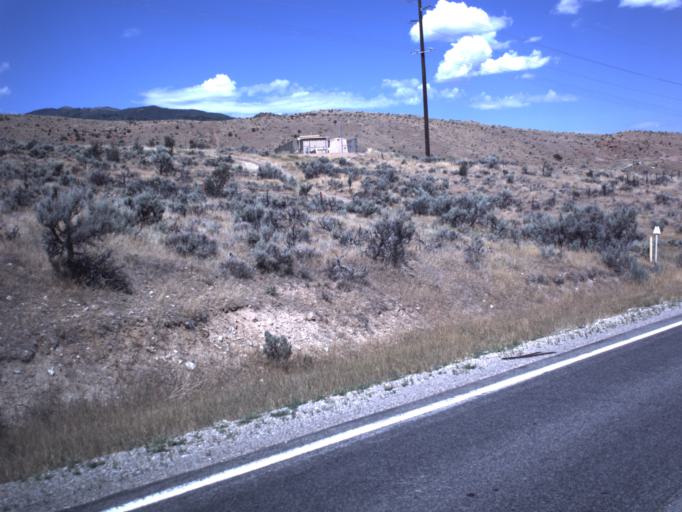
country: US
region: Utah
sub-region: Summit County
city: Coalville
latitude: 40.7973
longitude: -111.4093
